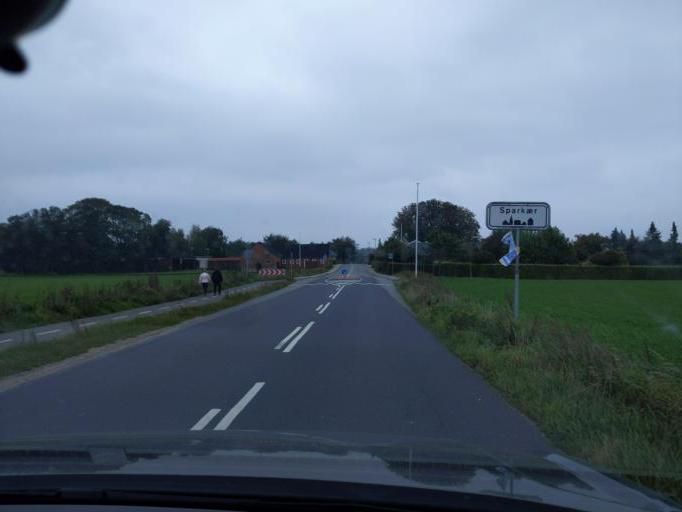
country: DK
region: Central Jutland
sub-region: Viborg Kommune
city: Stoholm
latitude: 56.4713
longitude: 9.2267
